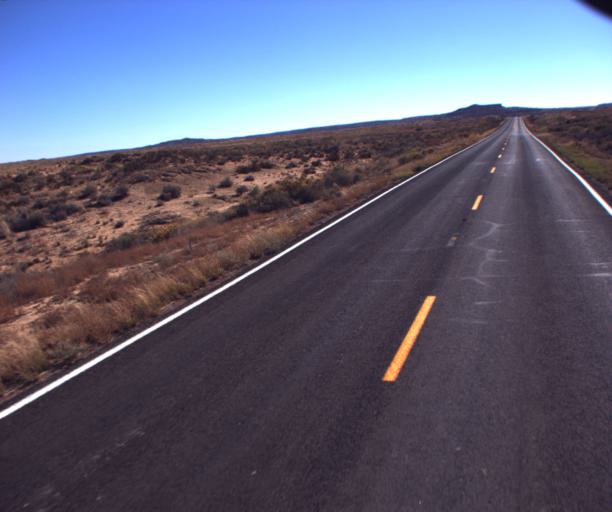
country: US
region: Arizona
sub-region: Navajo County
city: First Mesa
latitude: 35.9805
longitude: -110.7045
